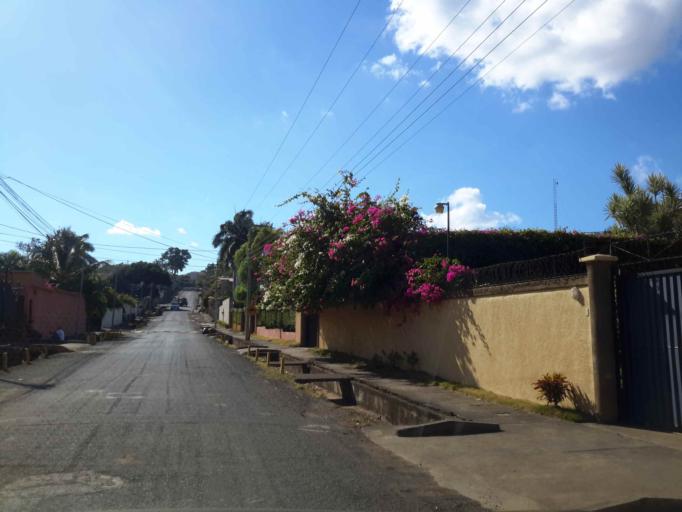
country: NI
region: Managua
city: Managua
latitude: 12.0802
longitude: -86.2379
